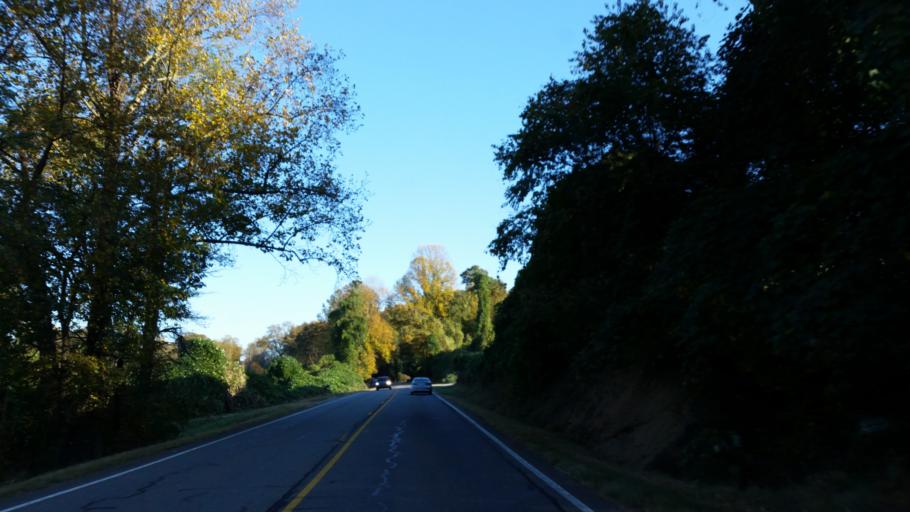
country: US
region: Georgia
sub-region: Pickens County
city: Jasper
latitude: 34.6043
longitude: -84.3482
